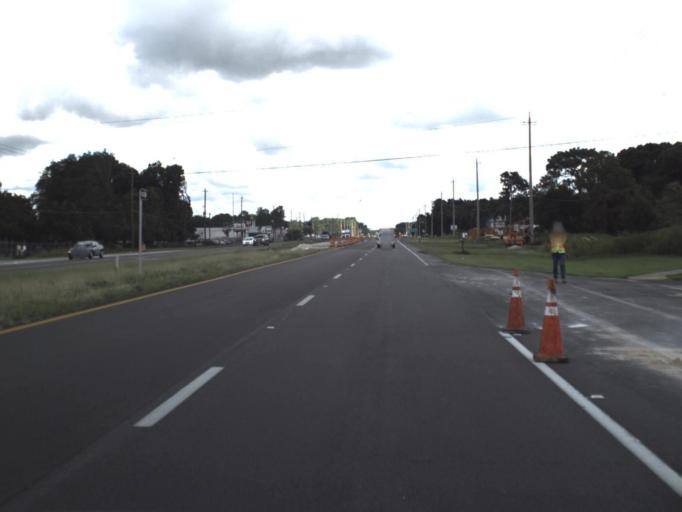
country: US
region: Florida
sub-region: Polk County
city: Gibsonia
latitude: 28.1432
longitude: -81.9736
